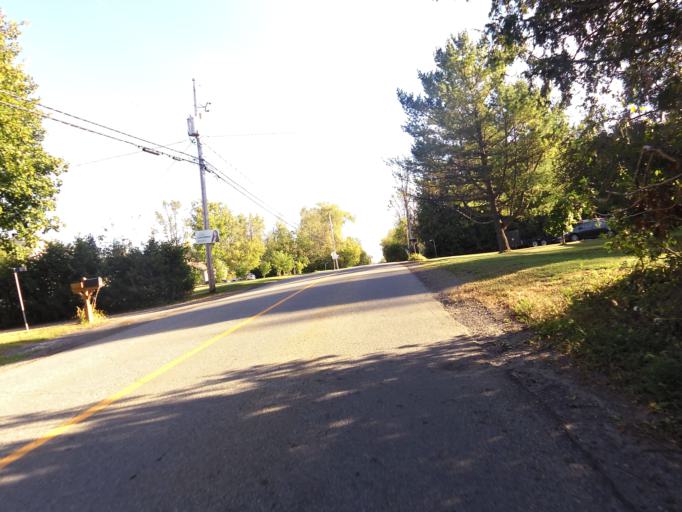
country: CA
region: Ontario
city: Bells Corners
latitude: 45.4368
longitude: -75.8802
